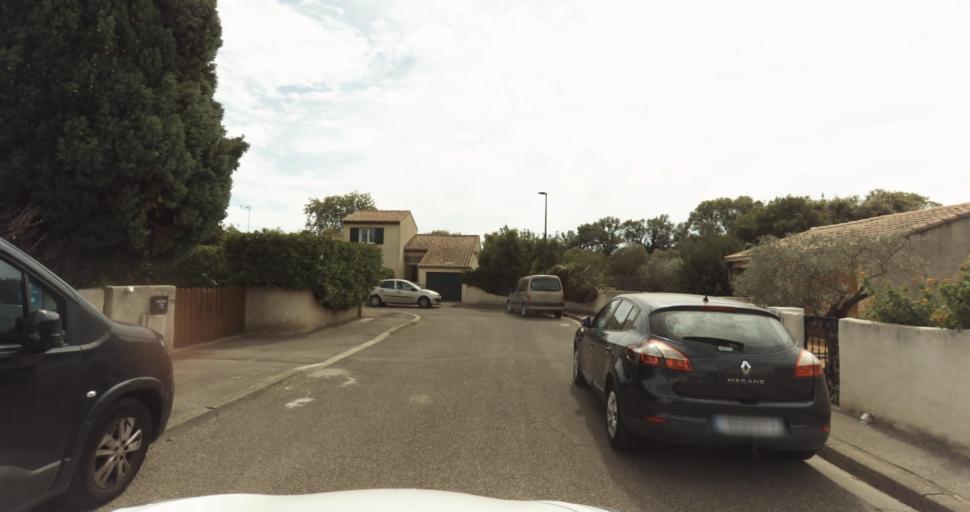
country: FR
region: Provence-Alpes-Cote d'Azur
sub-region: Departement des Bouches-du-Rhone
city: Miramas
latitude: 43.5765
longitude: 4.9925
